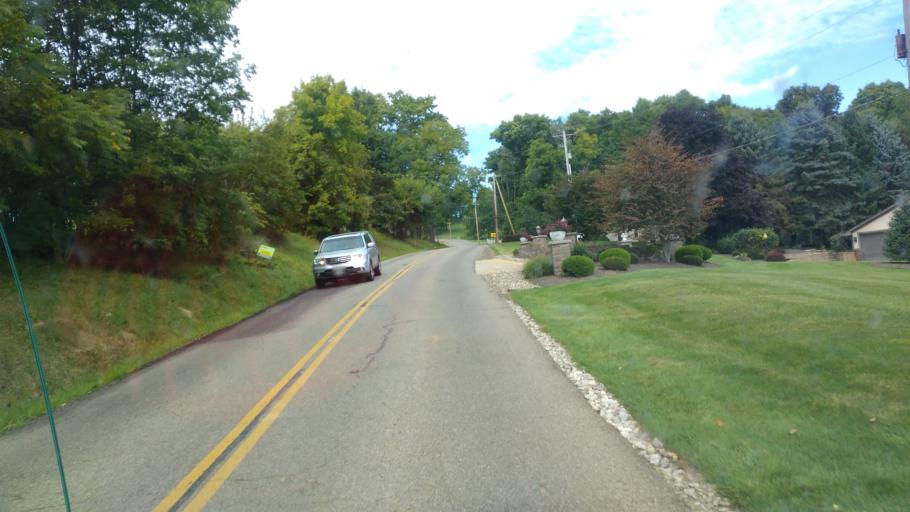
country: US
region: Ohio
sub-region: Holmes County
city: Millersburg
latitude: 40.5562
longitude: -81.8062
